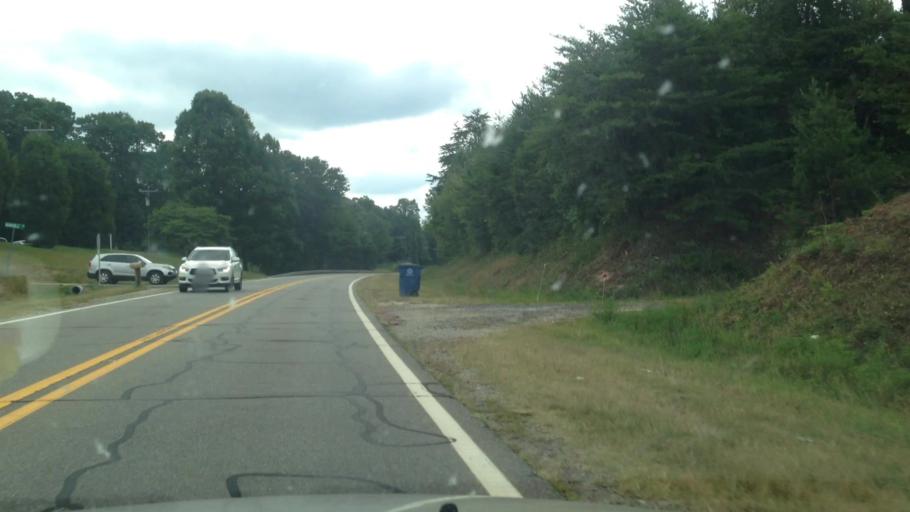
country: US
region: North Carolina
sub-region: Rockingham County
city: Madison
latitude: 36.3824
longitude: -79.9173
